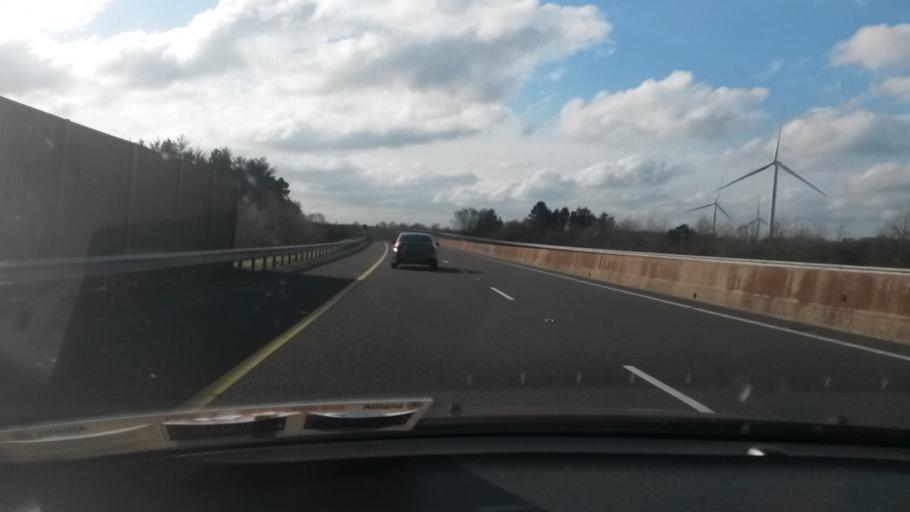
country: IE
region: Munster
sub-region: North Tipperary
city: Roscrea
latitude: 52.9212
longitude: -7.7262
